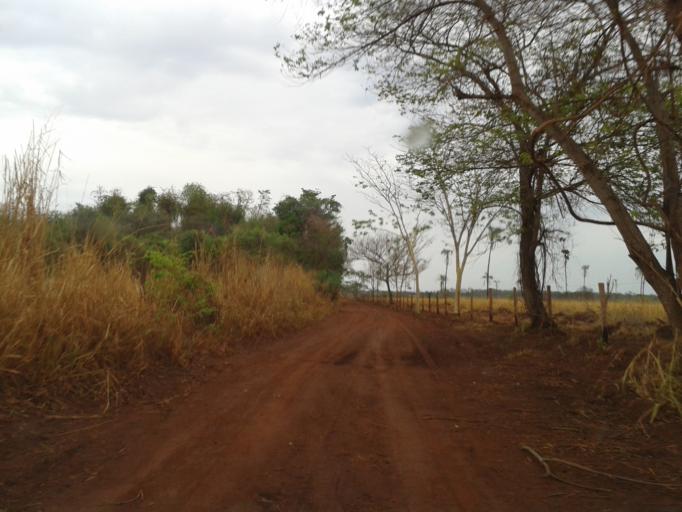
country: BR
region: Minas Gerais
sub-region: Capinopolis
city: Capinopolis
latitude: -18.8746
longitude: -49.7919
